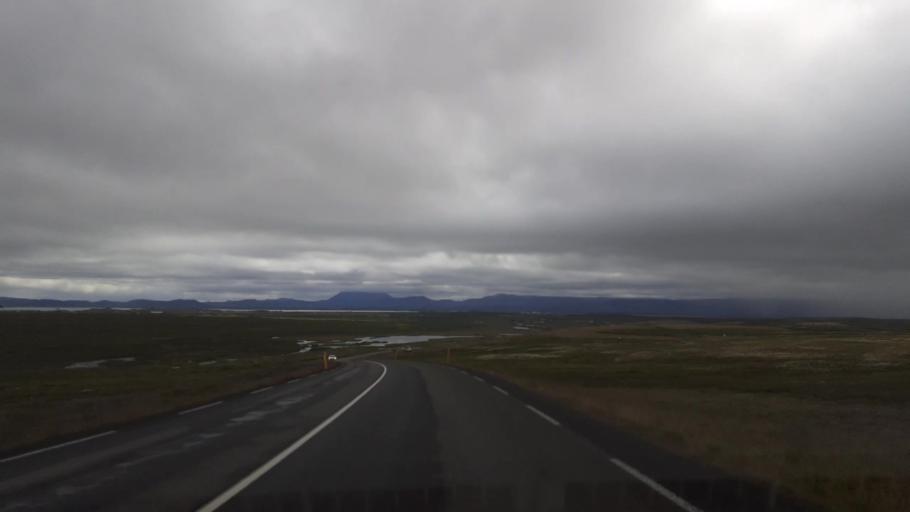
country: IS
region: Northeast
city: Laugar
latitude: 65.5954
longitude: -17.1909
